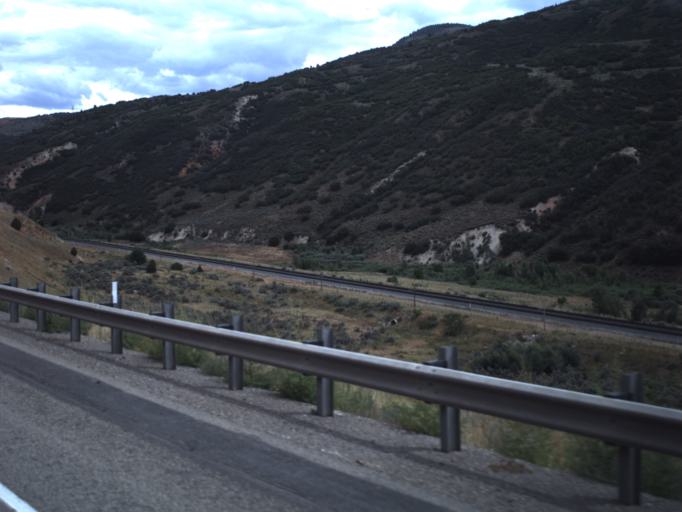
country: US
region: Utah
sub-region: Utah County
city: Mapleton
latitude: 39.9953
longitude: -111.4602
